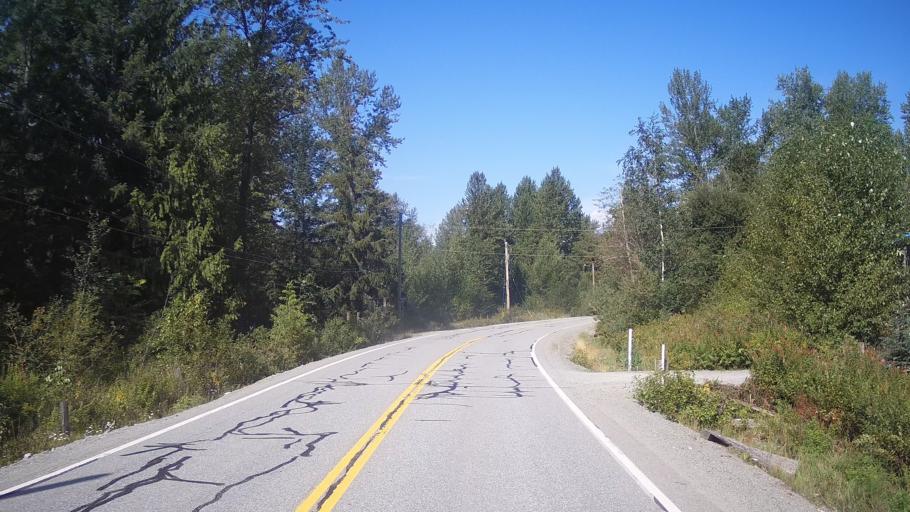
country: CA
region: British Columbia
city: Pemberton
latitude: 50.3074
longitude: -122.6136
